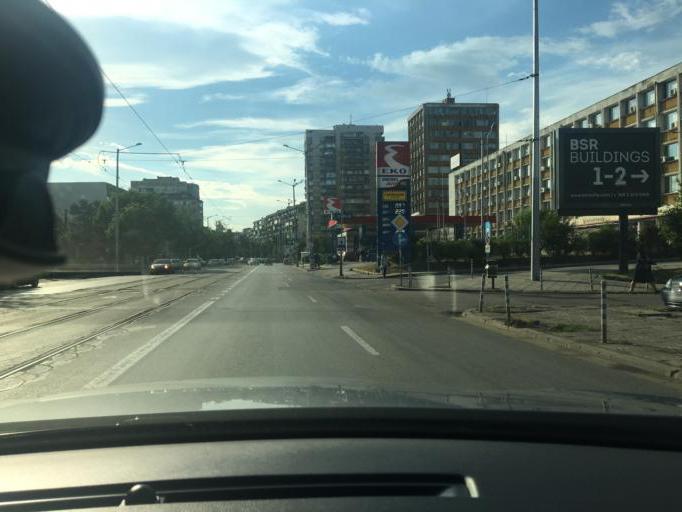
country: BG
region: Sofia-Capital
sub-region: Stolichna Obshtina
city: Sofia
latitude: 42.6775
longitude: 23.3678
